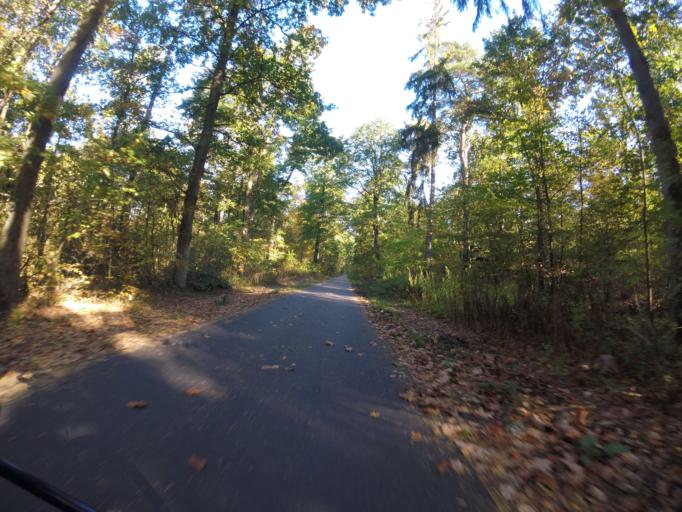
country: DE
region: Baden-Wuerttemberg
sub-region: Karlsruhe Region
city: Karlsruhe
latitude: 49.0387
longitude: 8.4070
